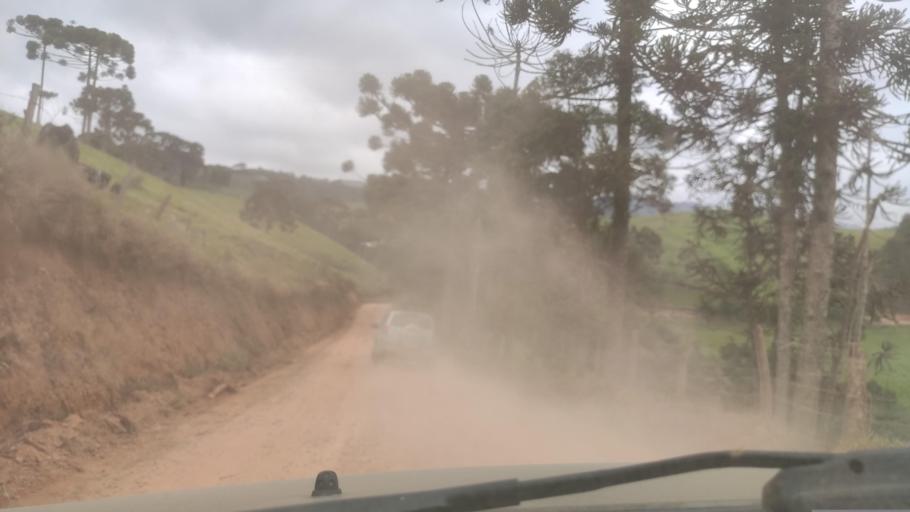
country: BR
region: Minas Gerais
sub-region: Paraisopolis
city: Paraisopolis
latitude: -22.6596
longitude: -45.8985
